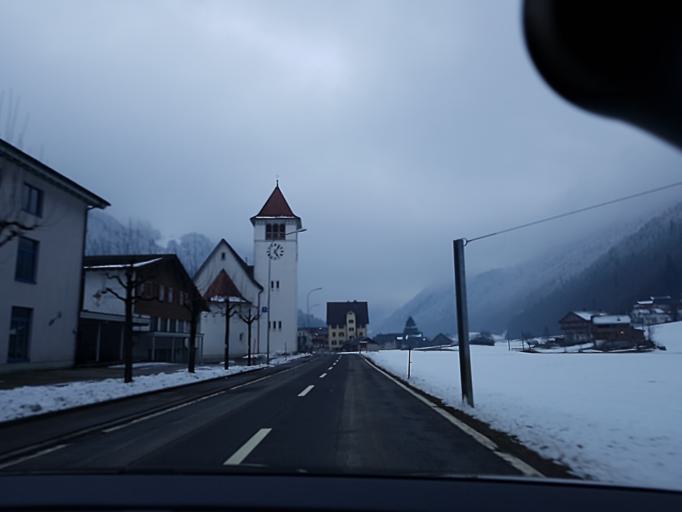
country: CH
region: Schwyz
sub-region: Bezirk Schwyz
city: Muotathal
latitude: 46.9865
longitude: 8.7150
